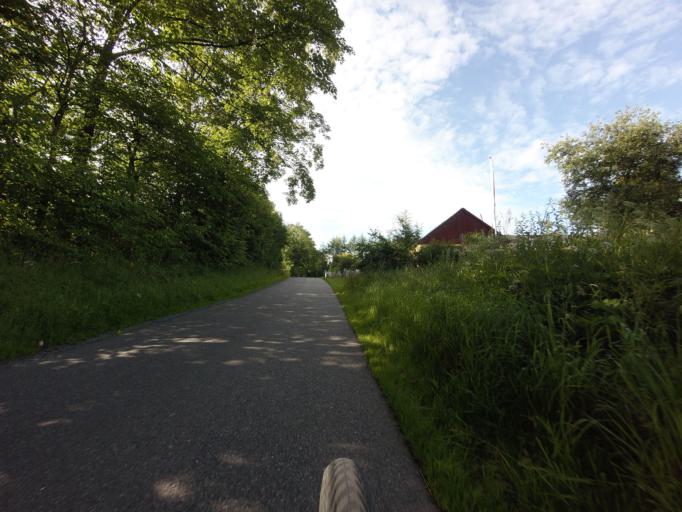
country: DK
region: Central Jutland
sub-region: Skanderborg Kommune
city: Stilling
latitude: 56.0734
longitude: 9.9648
